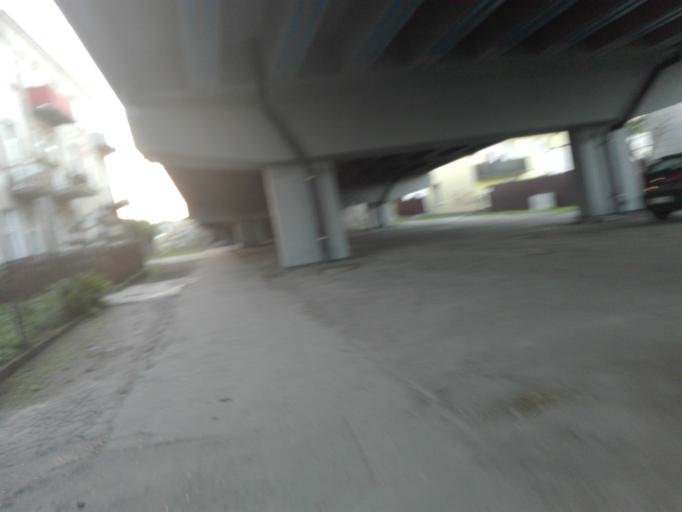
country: PL
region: Masovian Voivodeship
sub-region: Powiat sochaczewski
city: Sochaczew
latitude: 52.2178
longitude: 20.2411
